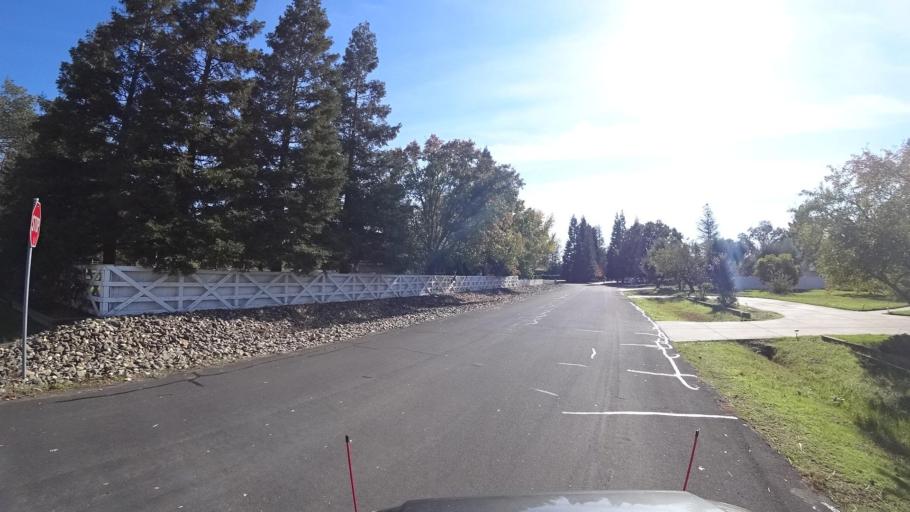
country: US
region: California
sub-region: Sacramento County
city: Vineyard
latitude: 38.4380
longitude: -121.3192
